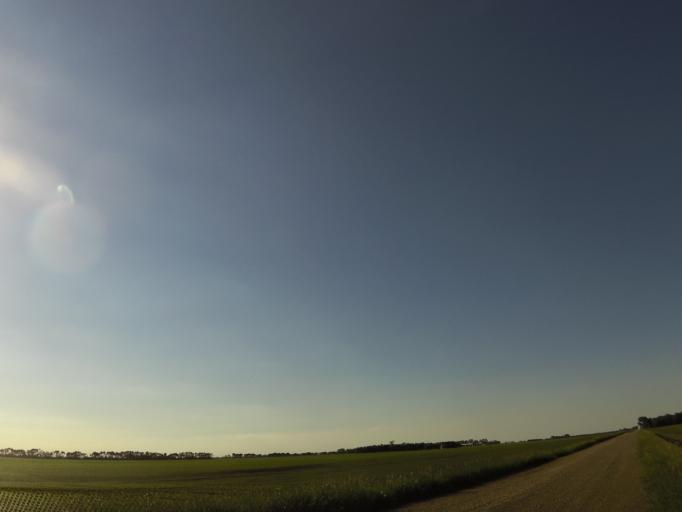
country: US
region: North Dakota
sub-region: Walsh County
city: Grafton
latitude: 48.3973
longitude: -97.2134
